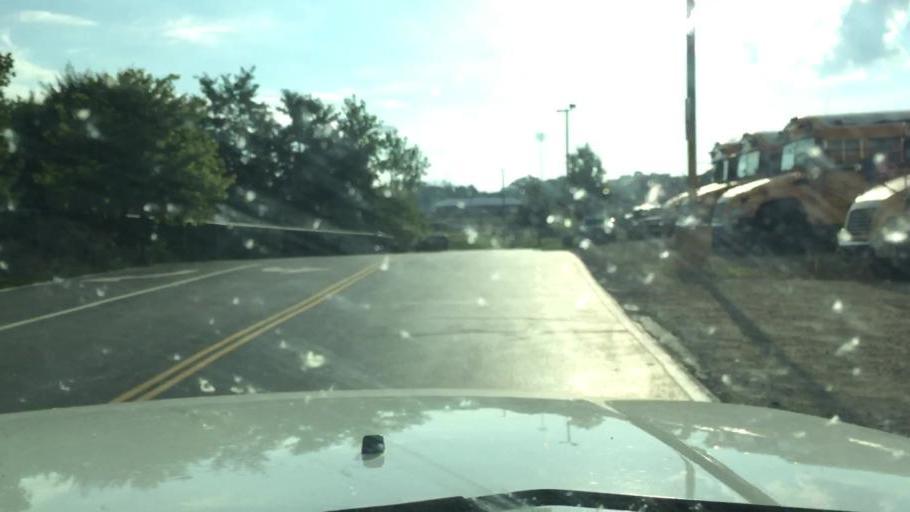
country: US
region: Ohio
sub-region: Champaign County
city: Mechanicsburg
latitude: 40.0779
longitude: -83.5633
